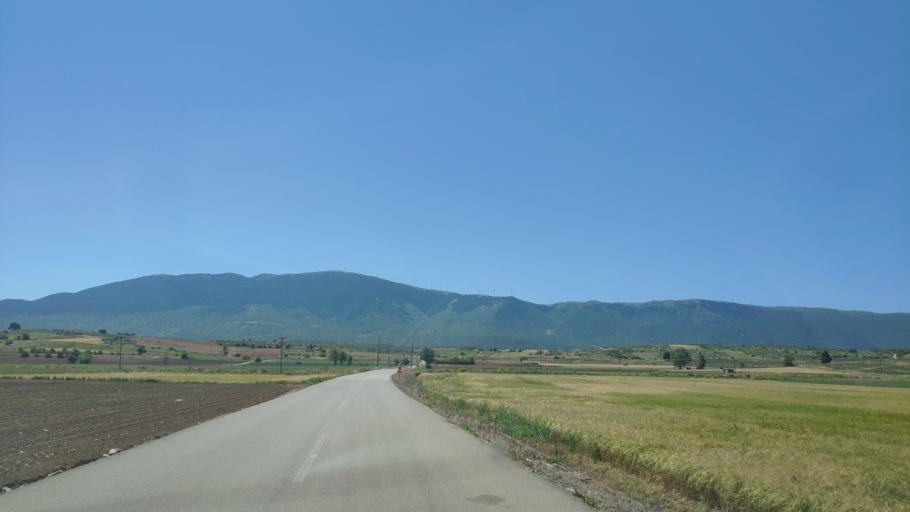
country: GR
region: Central Greece
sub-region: Nomos Voiotias
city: Kaparellion
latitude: 38.2610
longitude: 23.2351
